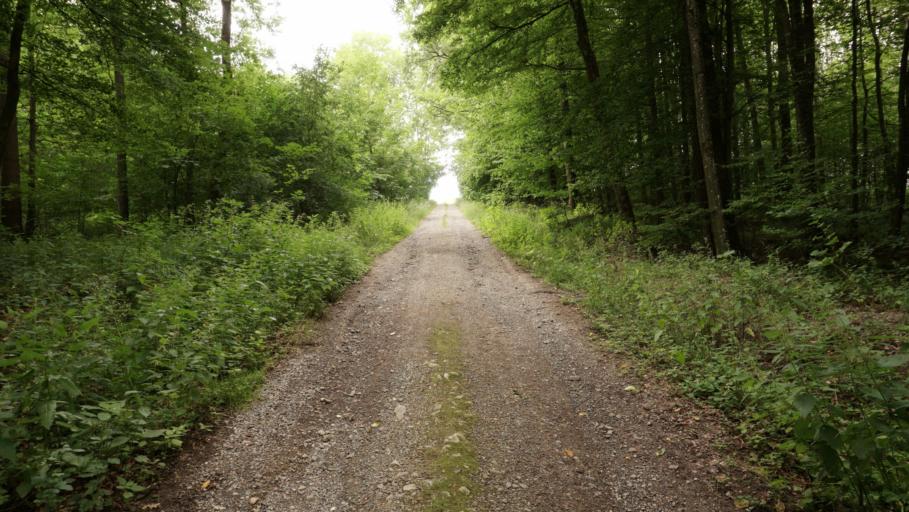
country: DE
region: Baden-Wuerttemberg
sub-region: Karlsruhe Region
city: Mosbach
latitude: 49.3303
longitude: 9.1723
